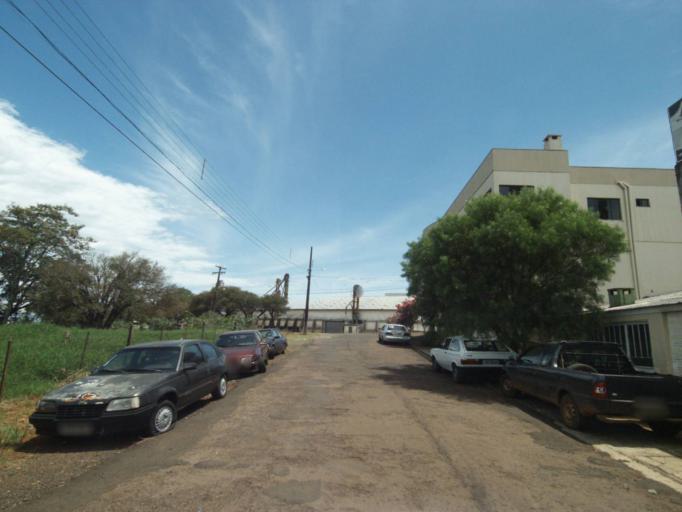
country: BR
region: Parana
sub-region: Guaraniacu
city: Guaraniacu
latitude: -25.1018
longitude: -52.8629
